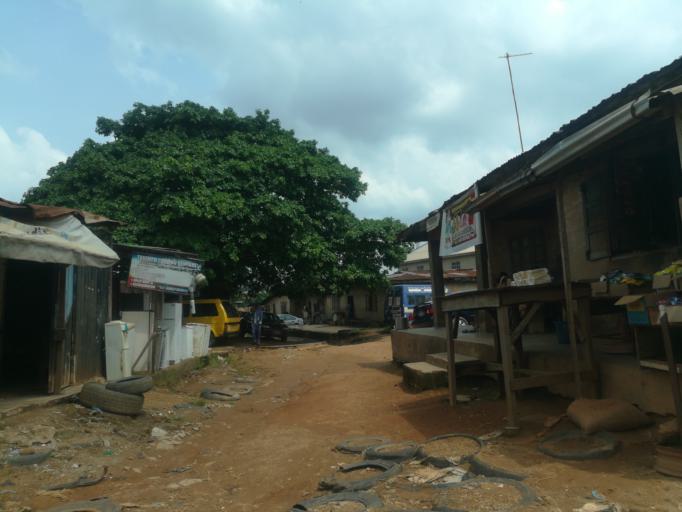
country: NG
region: Oyo
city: Ibadan
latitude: 7.4467
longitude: 3.9519
